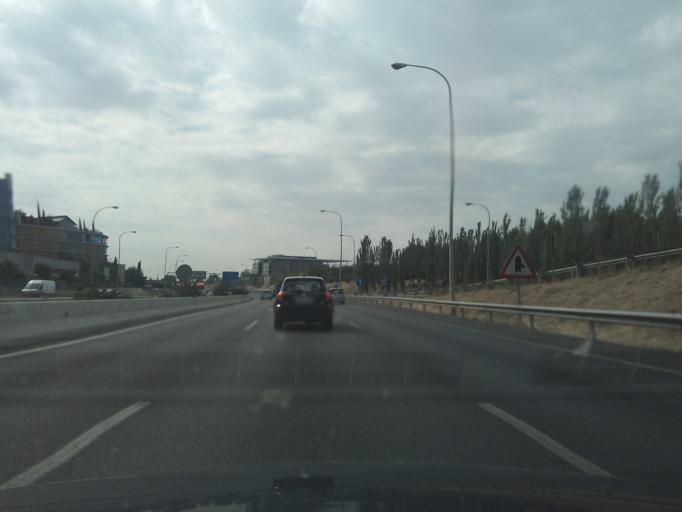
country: ES
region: Madrid
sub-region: Provincia de Madrid
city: Hortaleza
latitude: 40.4620
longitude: -3.6229
